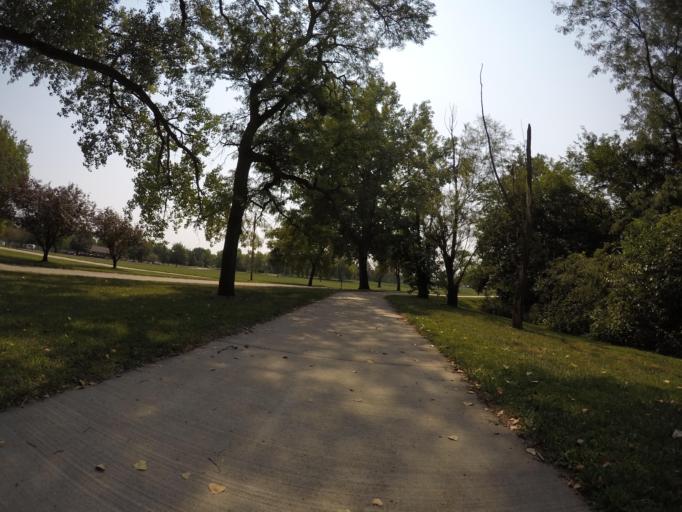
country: US
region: Nebraska
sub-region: Gage County
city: Beatrice
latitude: 40.2742
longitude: -96.7701
